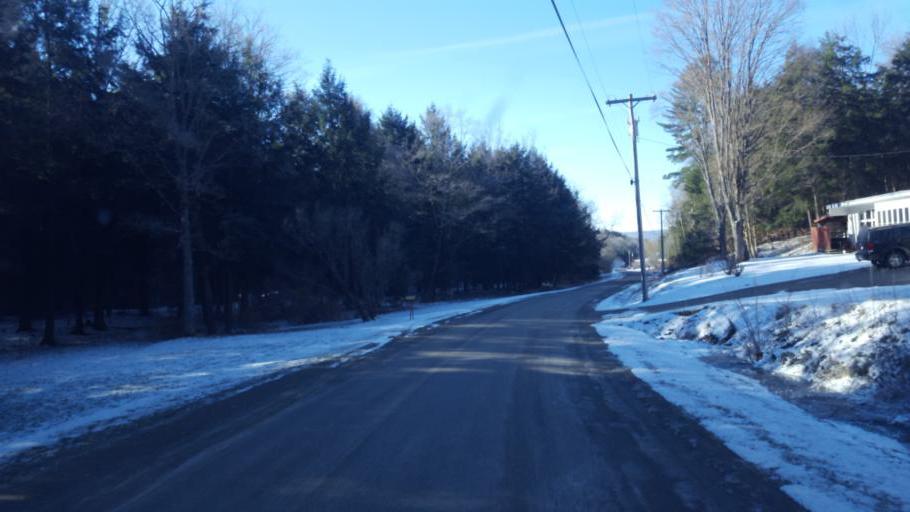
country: US
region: New York
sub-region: Allegany County
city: Wellsville
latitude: 42.1451
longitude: -77.9068
